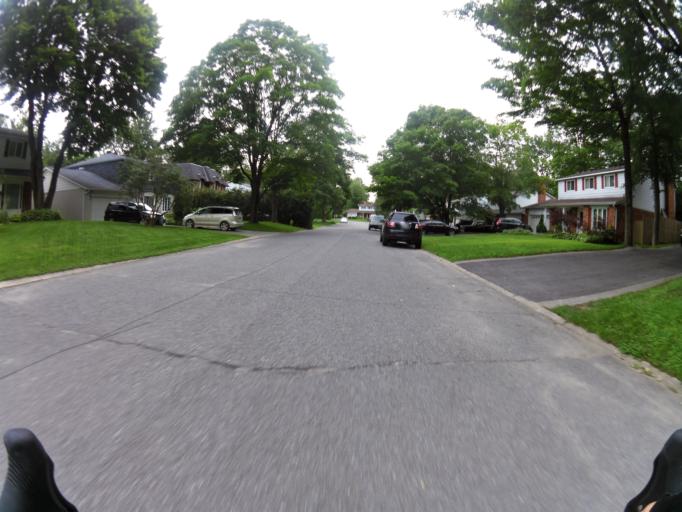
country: CA
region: Ontario
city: Ottawa
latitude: 45.3199
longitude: -75.7147
